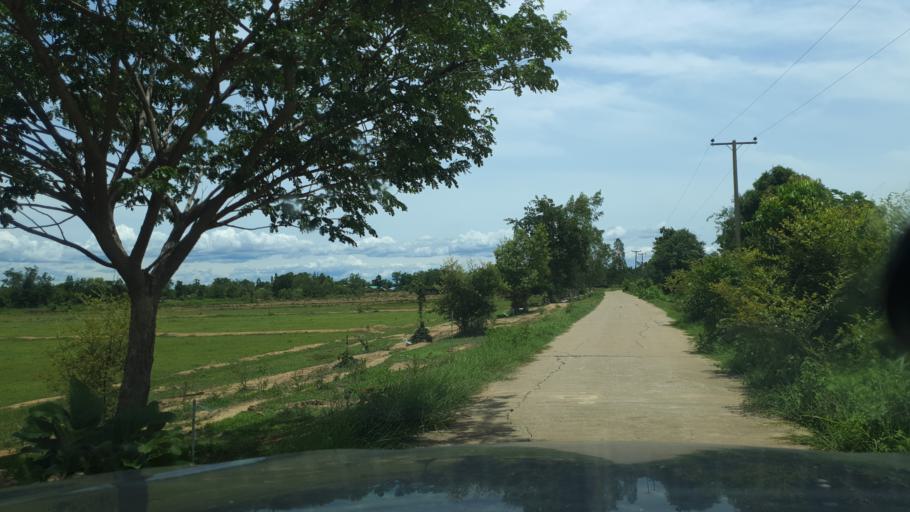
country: TH
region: Sukhothai
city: Ban Na
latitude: 17.0893
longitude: 99.6870
